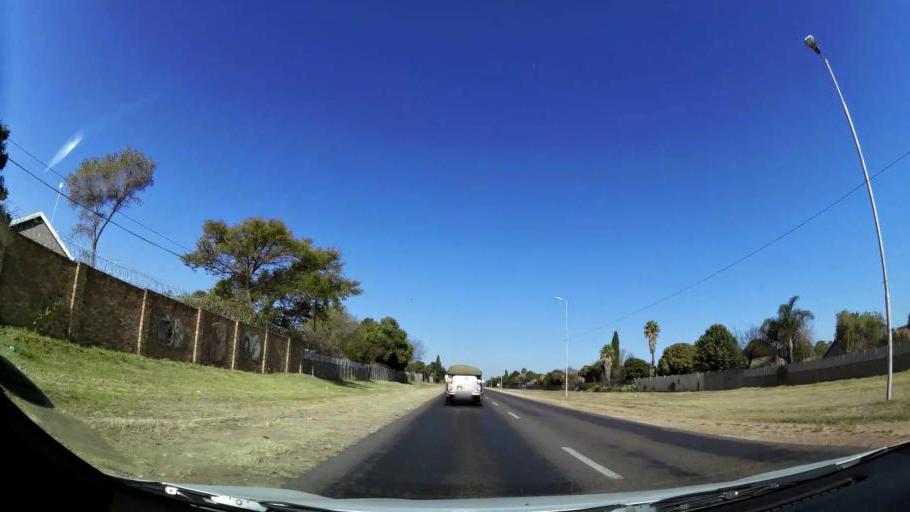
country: ZA
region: Gauteng
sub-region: City of Tshwane Metropolitan Municipality
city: Centurion
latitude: -25.8313
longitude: 28.2654
